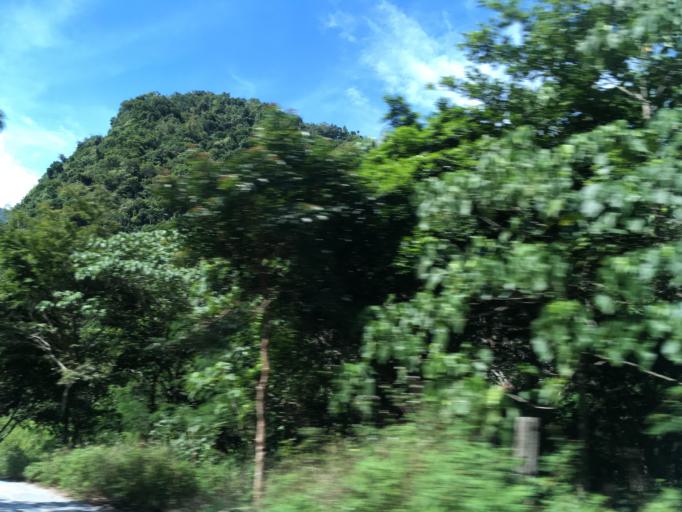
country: TW
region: Taiwan
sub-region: Yilan
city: Yilan
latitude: 24.4346
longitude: 121.7511
